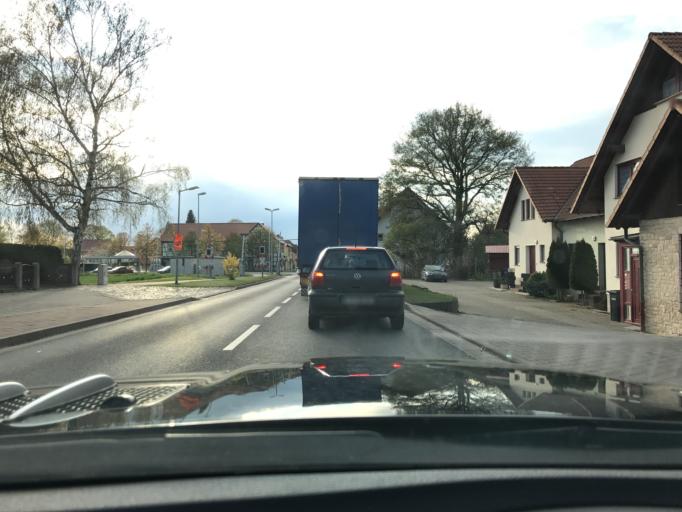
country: DE
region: Thuringia
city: Grossvargula
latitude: 51.0903
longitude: 10.7354
